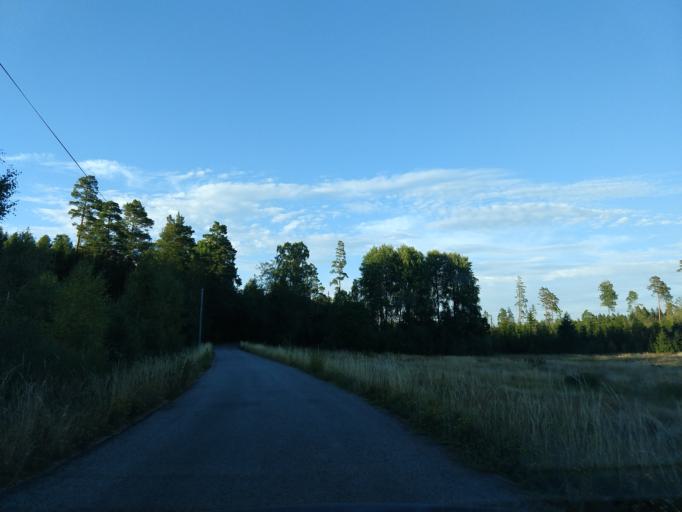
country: SE
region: Blekinge
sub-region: Ronneby Kommun
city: Brakne-Hoby
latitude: 56.2638
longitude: 15.1426
